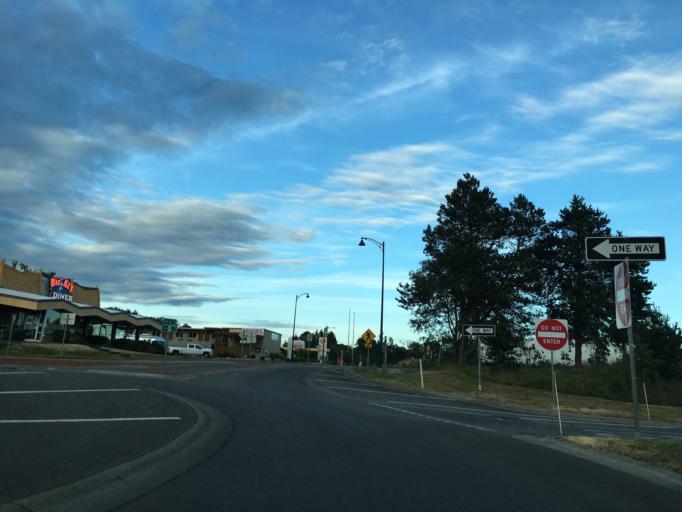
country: US
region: Washington
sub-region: Whatcom County
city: Blaine
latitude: 48.9980
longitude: -122.7517
